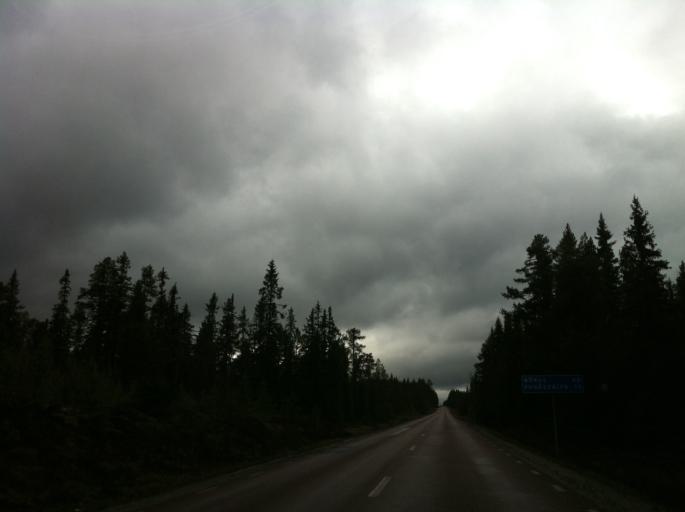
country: NO
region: Hedmark
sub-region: Engerdal
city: Engerdal
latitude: 62.4366
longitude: 12.7136
